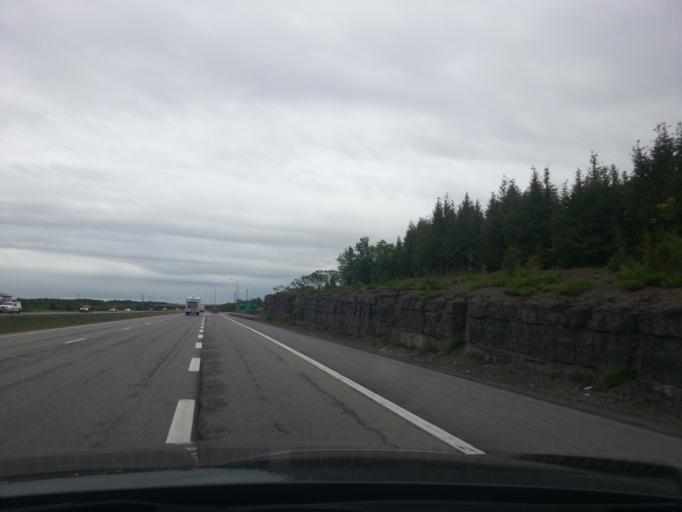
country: CA
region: Ontario
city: Bells Corners
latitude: 45.2762
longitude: -75.8007
